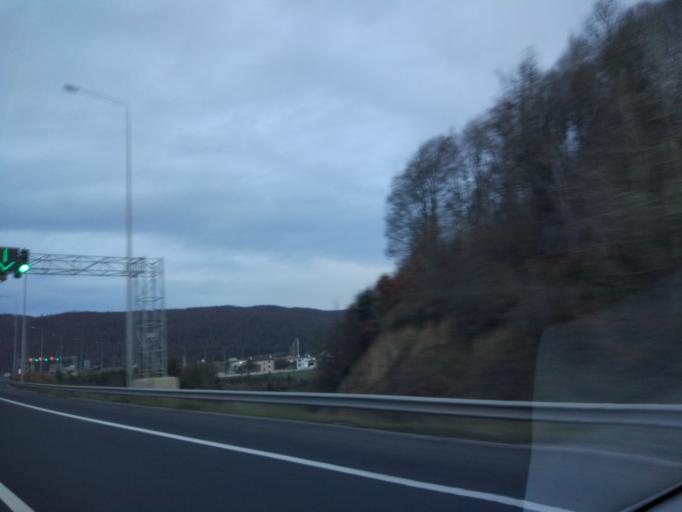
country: TR
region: Duzce
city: Kaynasli
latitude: 40.7282
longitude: 31.4447
